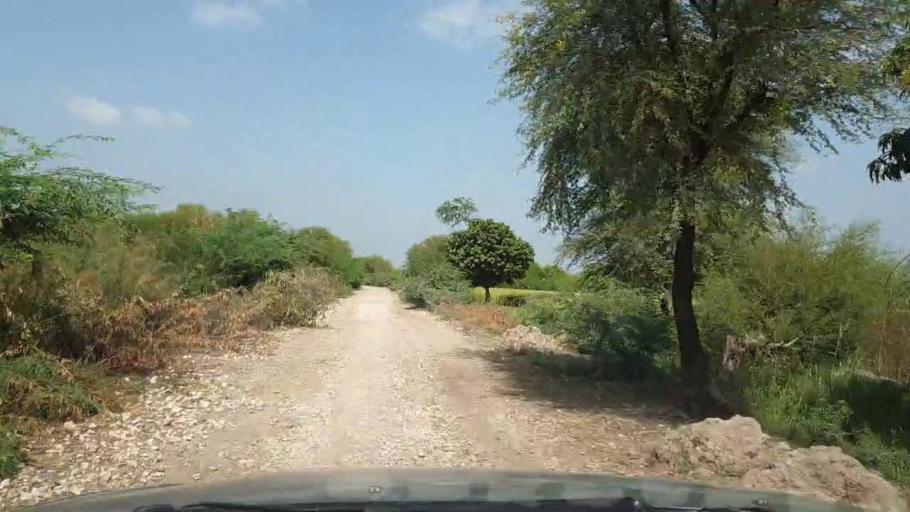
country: PK
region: Sindh
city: Rajo Khanani
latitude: 25.0289
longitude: 68.9166
